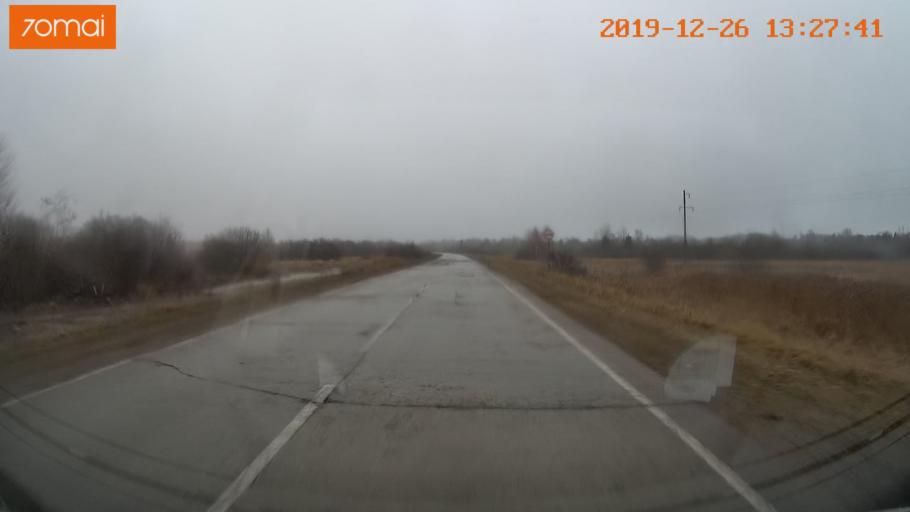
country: RU
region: Vologda
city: Cherepovets
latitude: 58.8521
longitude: 38.2420
